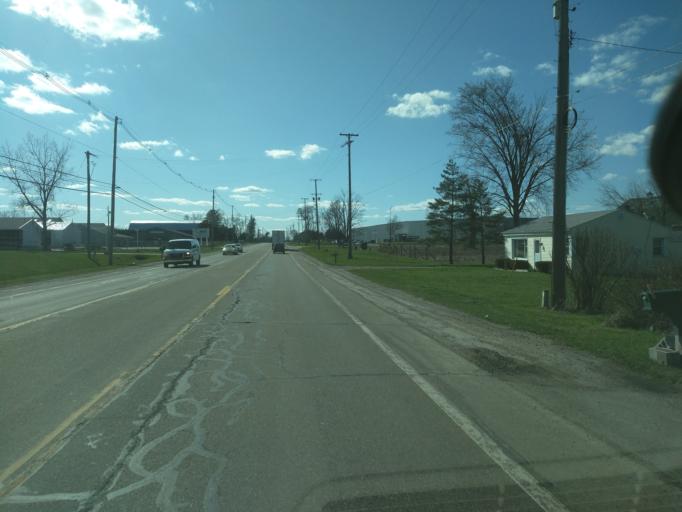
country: US
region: Michigan
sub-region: Eaton County
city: Waverly
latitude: 42.7766
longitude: -84.6267
